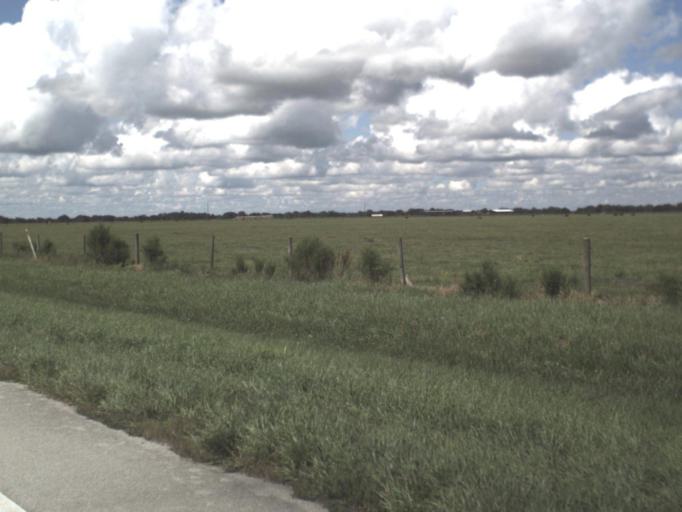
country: US
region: Florida
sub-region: DeSoto County
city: Arcadia
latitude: 27.2423
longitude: -81.9452
